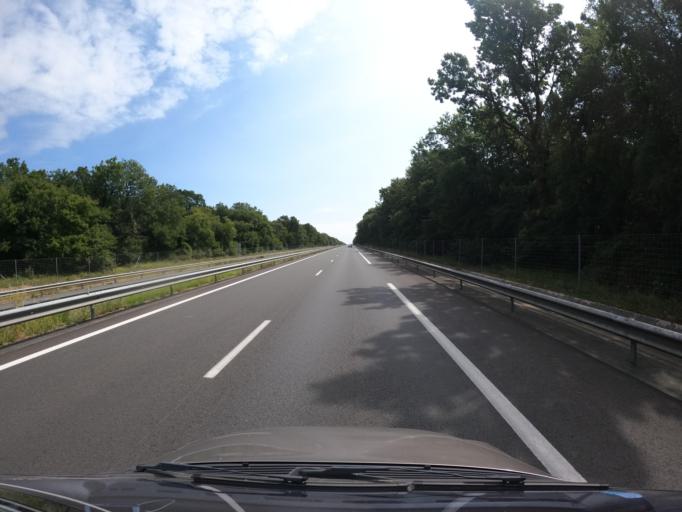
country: FR
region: Poitou-Charentes
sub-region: Departement de la Charente-Maritime
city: Courcon
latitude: 46.2202
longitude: -0.8003
